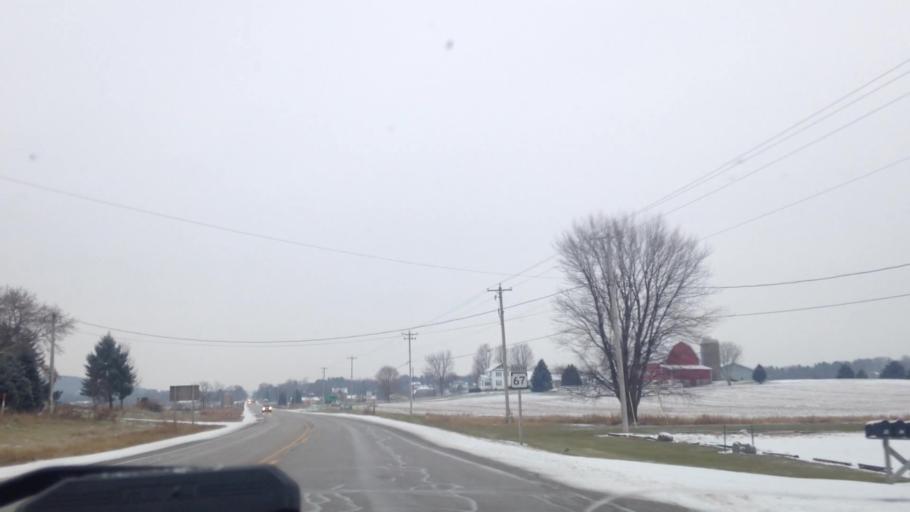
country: US
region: Wisconsin
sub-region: Dodge County
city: Hustisford
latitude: 43.3260
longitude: -88.5183
